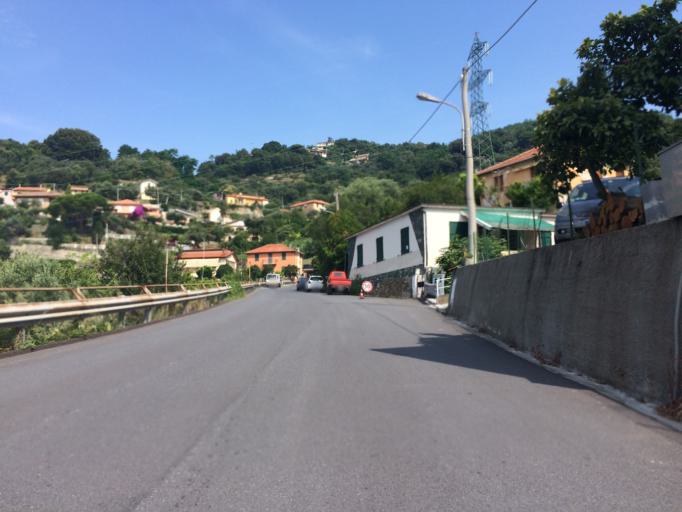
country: IT
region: Liguria
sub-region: Provincia di Savona
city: Varazze
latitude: 44.3766
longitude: 8.5752
